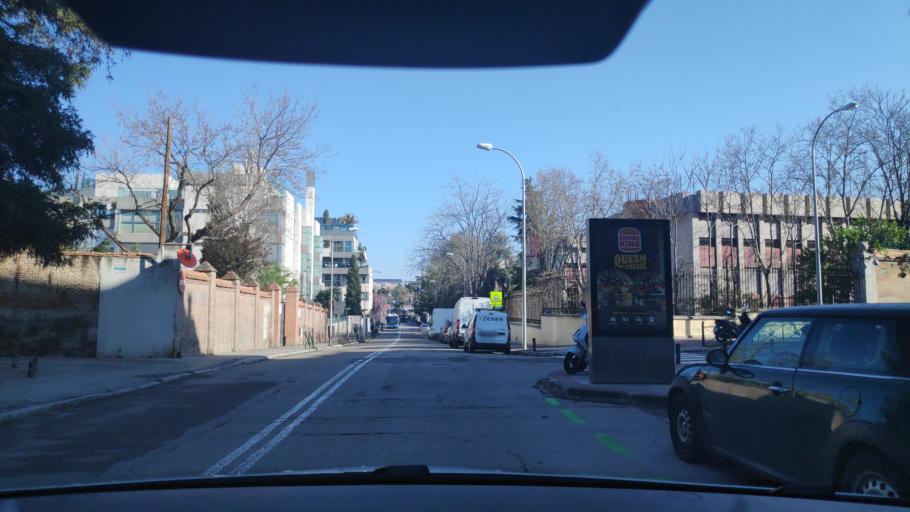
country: ES
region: Madrid
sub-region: Provincia de Madrid
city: Chamartin
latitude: 40.4651
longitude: -3.6795
